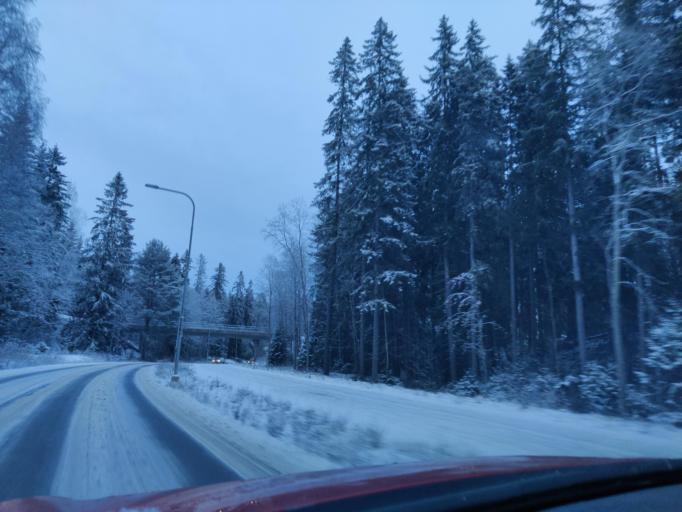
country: FI
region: Pirkanmaa
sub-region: Tampere
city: Tampere
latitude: 61.5107
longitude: 23.7947
